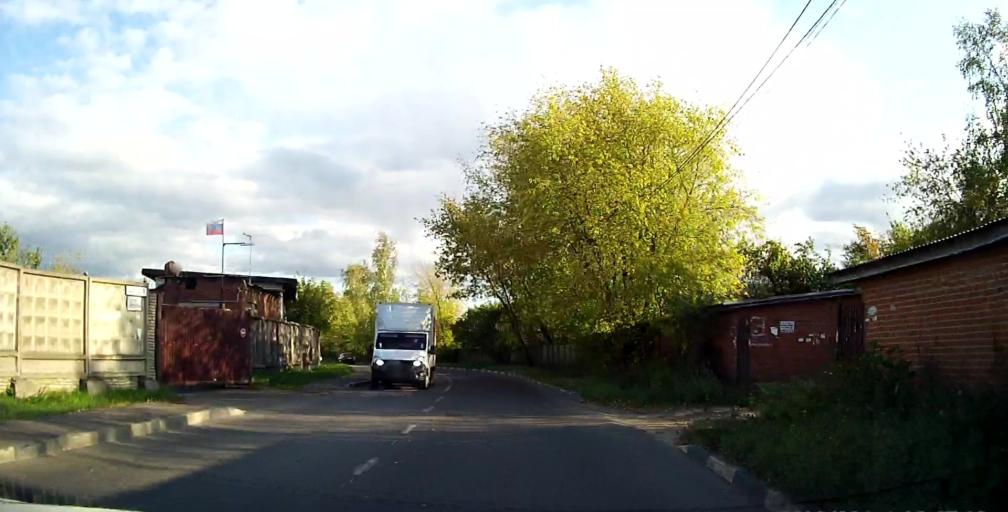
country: RU
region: Moskovskaya
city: Klimovsk
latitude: 55.3665
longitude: 37.5477
